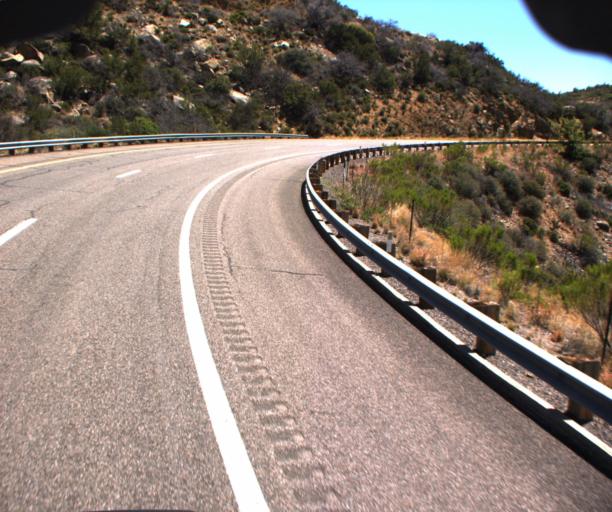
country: US
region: Arizona
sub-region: Yavapai County
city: Congress
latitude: 34.2040
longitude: -112.7608
